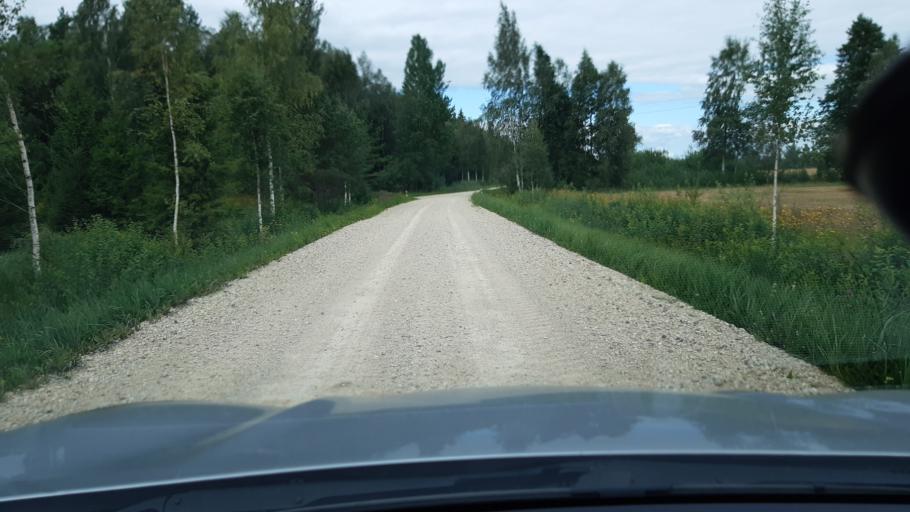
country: EE
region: Raplamaa
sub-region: Jaervakandi vald
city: Jarvakandi
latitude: 58.8002
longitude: 24.8598
